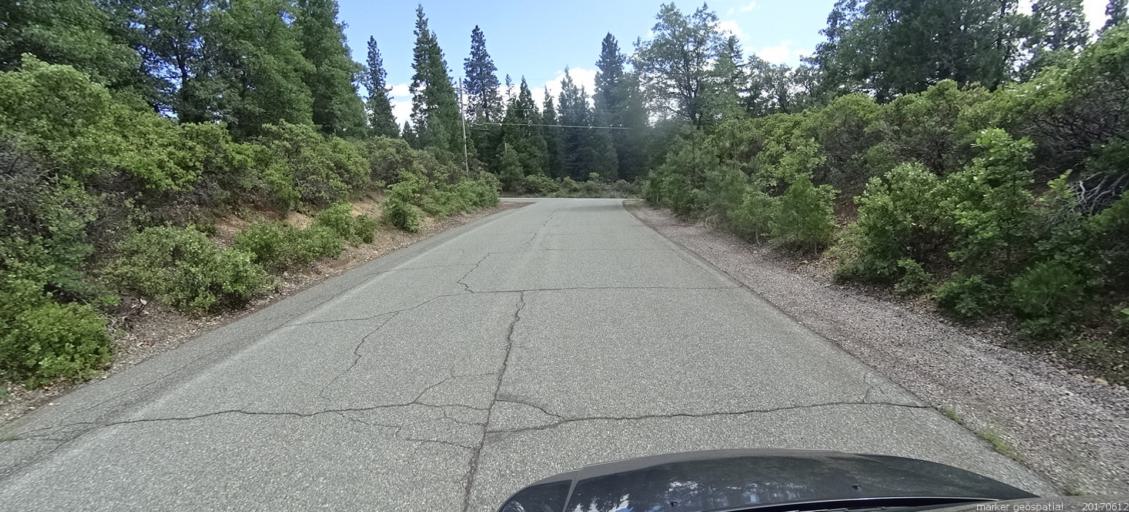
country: US
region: California
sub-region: Siskiyou County
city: Mount Shasta
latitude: 41.3000
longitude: -122.2930
